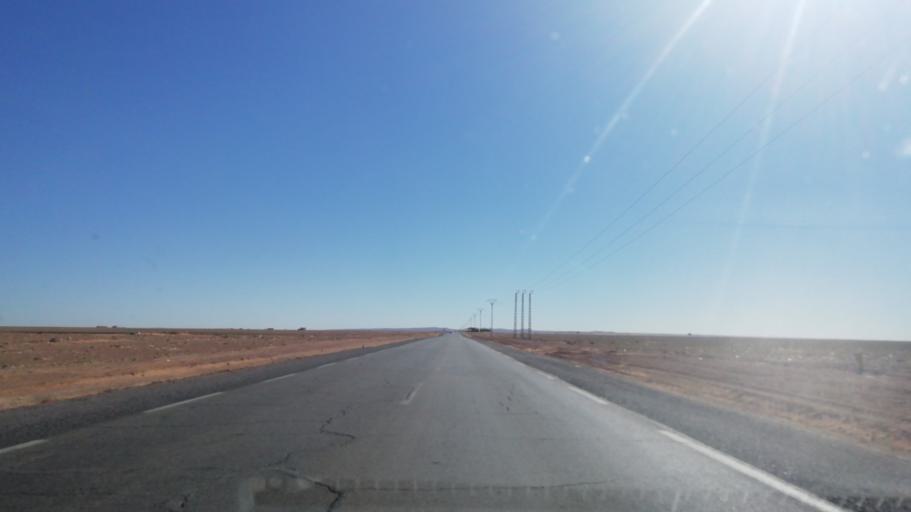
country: DZ
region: Saida
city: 'Ain el Hadjar
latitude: 34.0171
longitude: 0.1089
